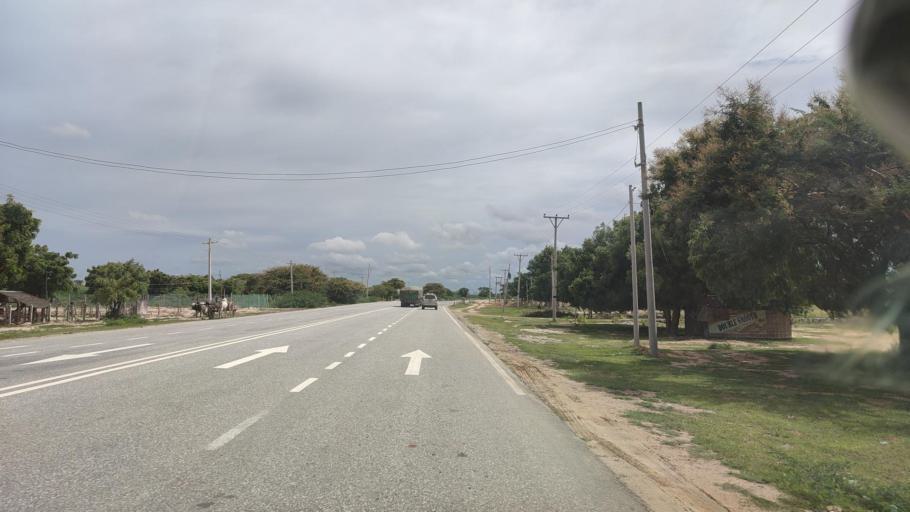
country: MM
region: Mandalay
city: Meiktila
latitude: 21.0427
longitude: 95.9959
